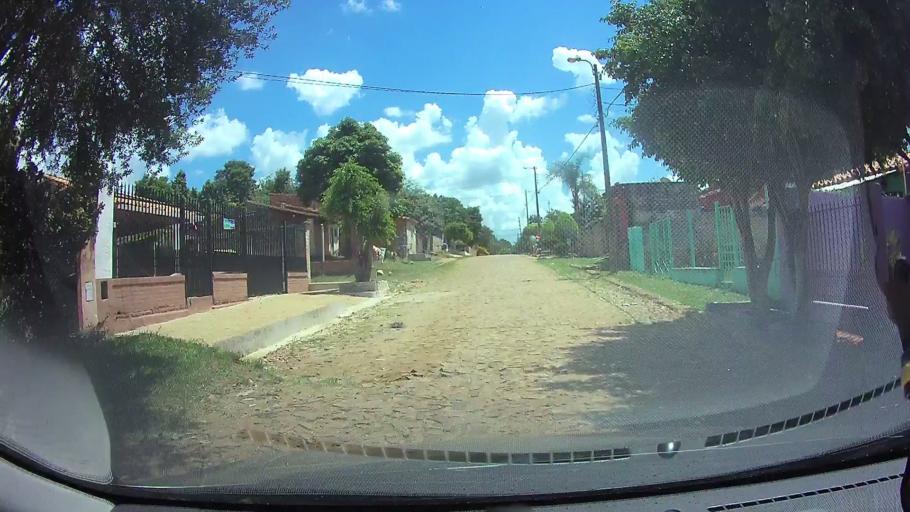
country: PY
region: Central
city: Limpio
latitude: -25.1516
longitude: -57.4465
